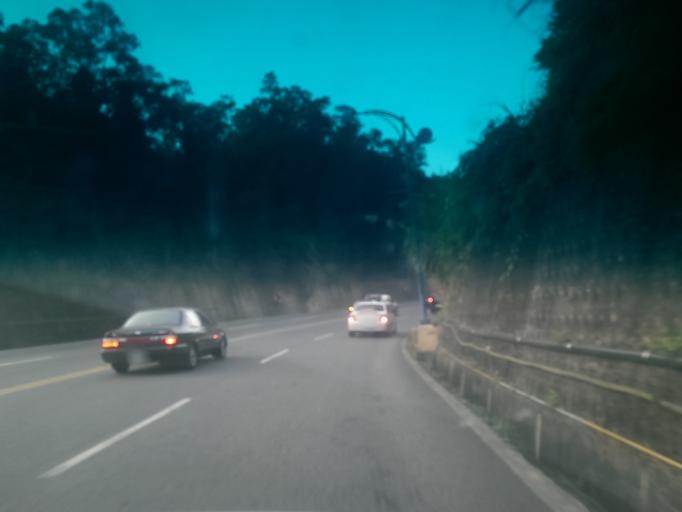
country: TW
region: Taiwan
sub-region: Nantou
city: Puli
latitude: 23.9314
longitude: 120.9223
